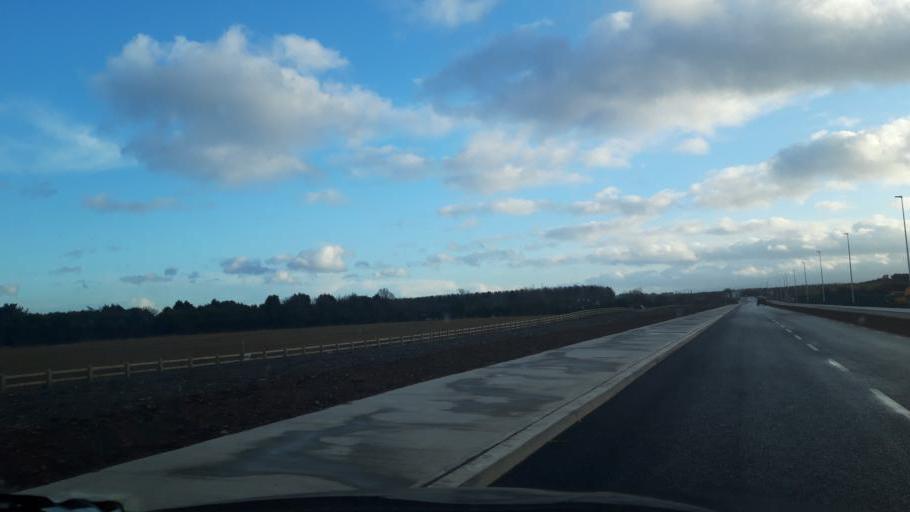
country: IE
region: Leinster
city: Donabate
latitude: 53.4867
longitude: -6.1366
